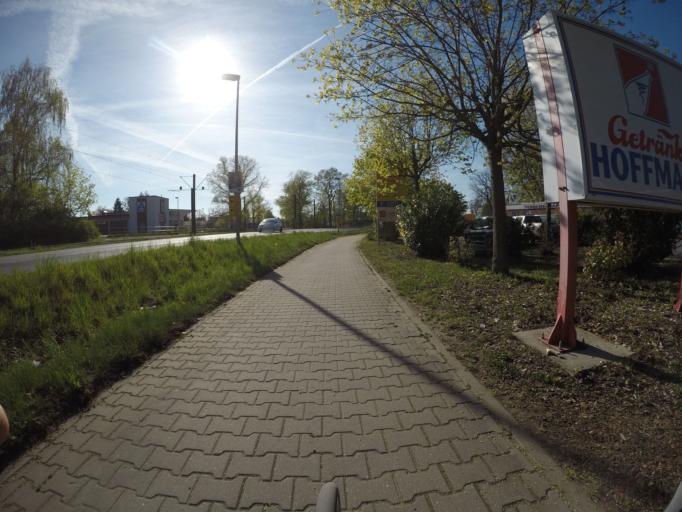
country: DE
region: Brandenburg
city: Schoneiche
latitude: 52.4736
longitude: 13.7148
